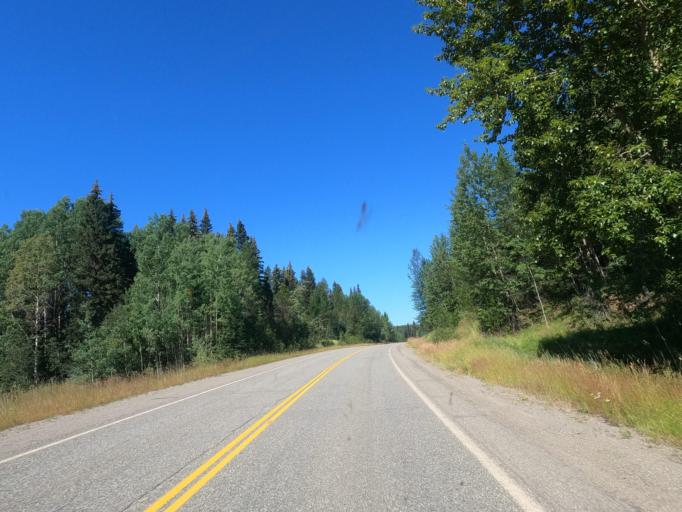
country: CA
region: British Columbia
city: Quesnel
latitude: 53.0538
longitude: -122.1621
